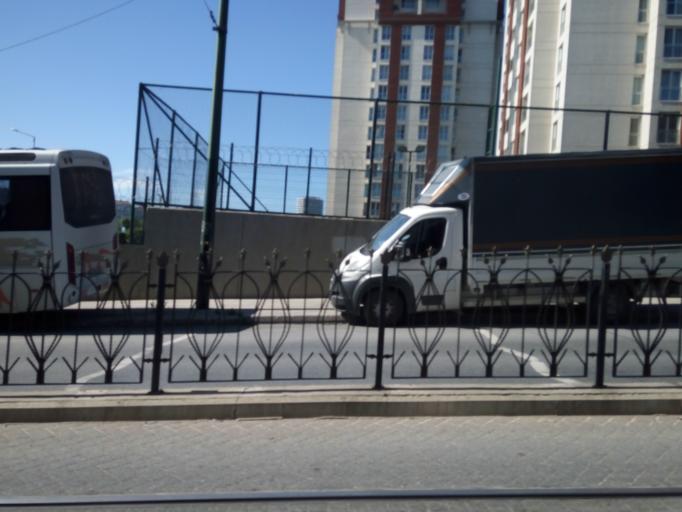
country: TR
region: Istanbul
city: guengoeren merter
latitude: 41.0019
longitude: 28.8953
